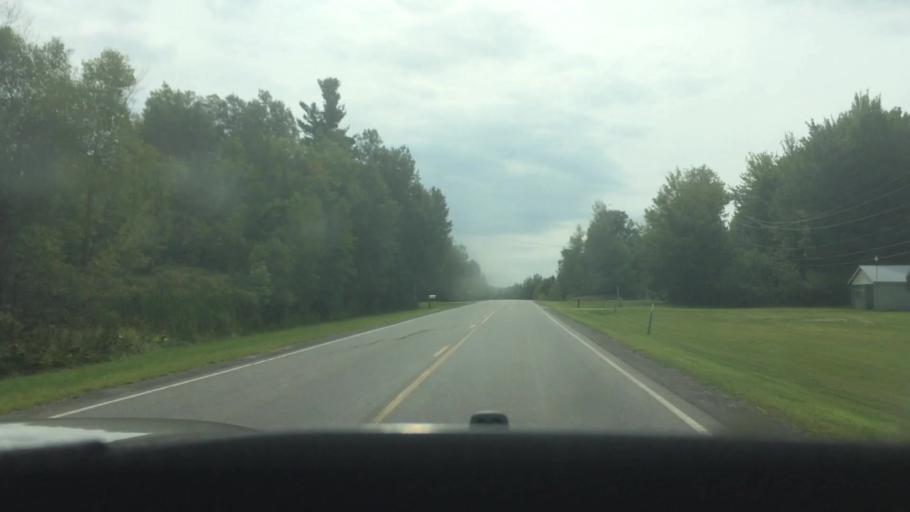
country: US
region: New York
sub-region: St. Lawrence County
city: Canton
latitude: 44.4986
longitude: -75.2655
